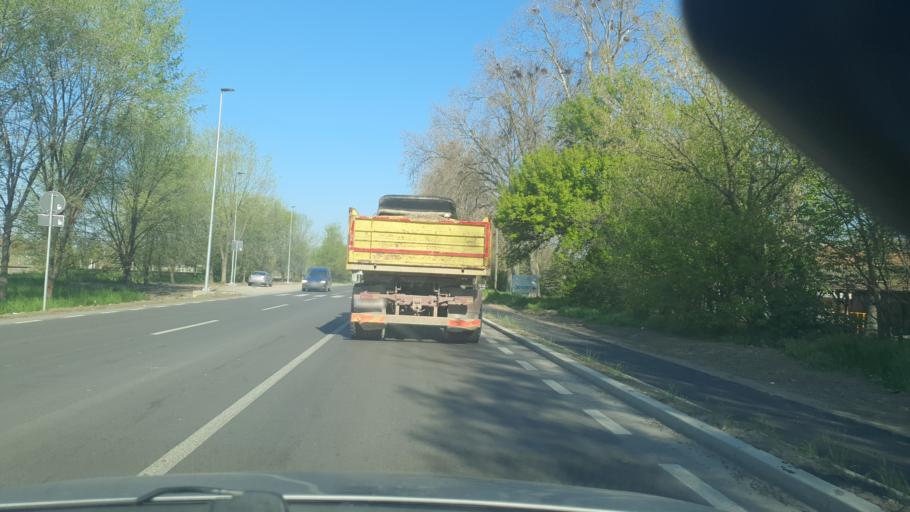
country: RS
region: Autonomna Pokrajina Vojvodina
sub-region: Juznobacki Okrug
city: Vrbas
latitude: 45.5878
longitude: 19.6017
